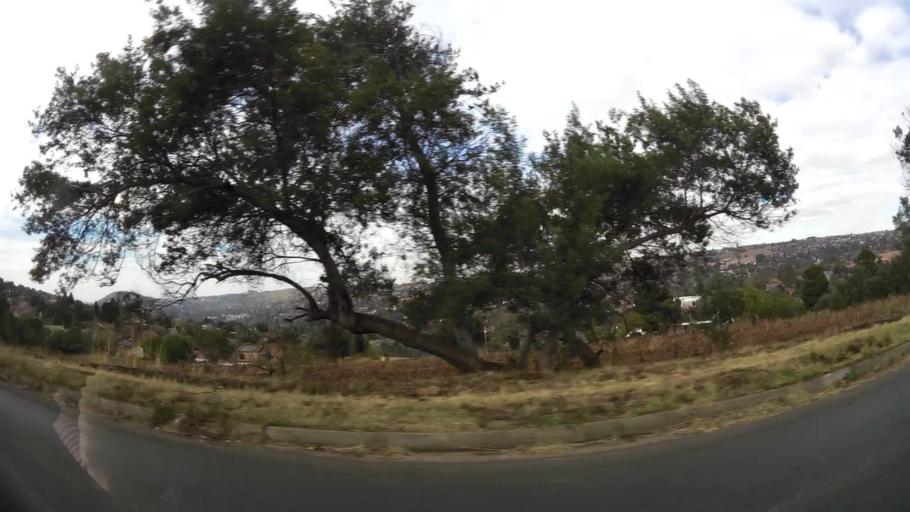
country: ZA
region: Gauteng
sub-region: City of Johannesburg Metropolitan Municipality
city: Roodepoort
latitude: -26.1074
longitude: 27.8621
